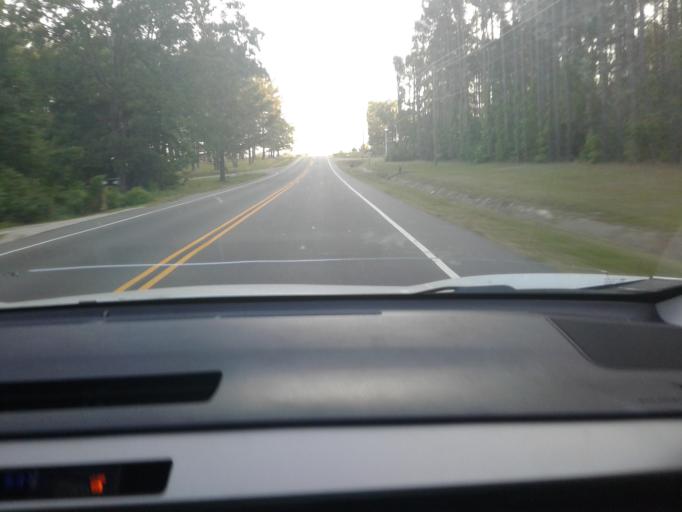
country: US
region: North Carolina
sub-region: Harnett County
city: Lillington
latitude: 35.4476
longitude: -78.8283
